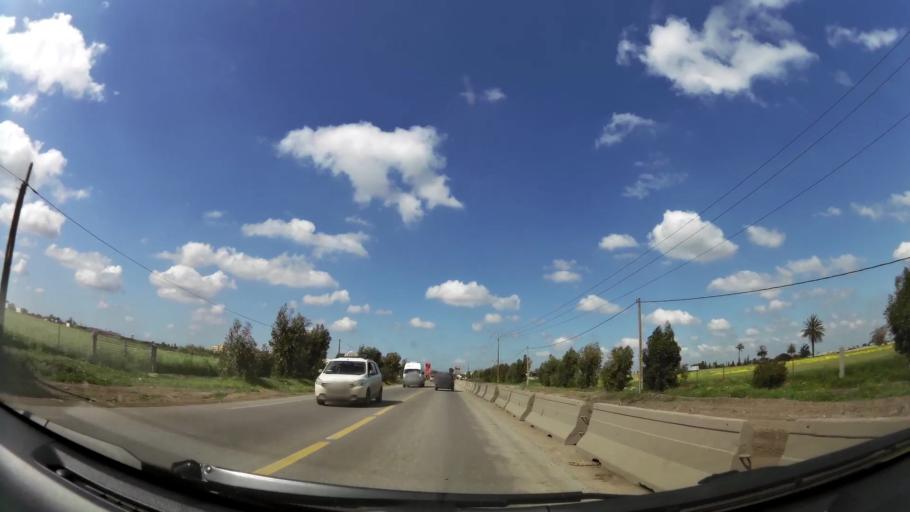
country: MA
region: Grand Casablanca
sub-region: Mediouna
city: Mediouna
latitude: 33.4287
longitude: -7.5226
